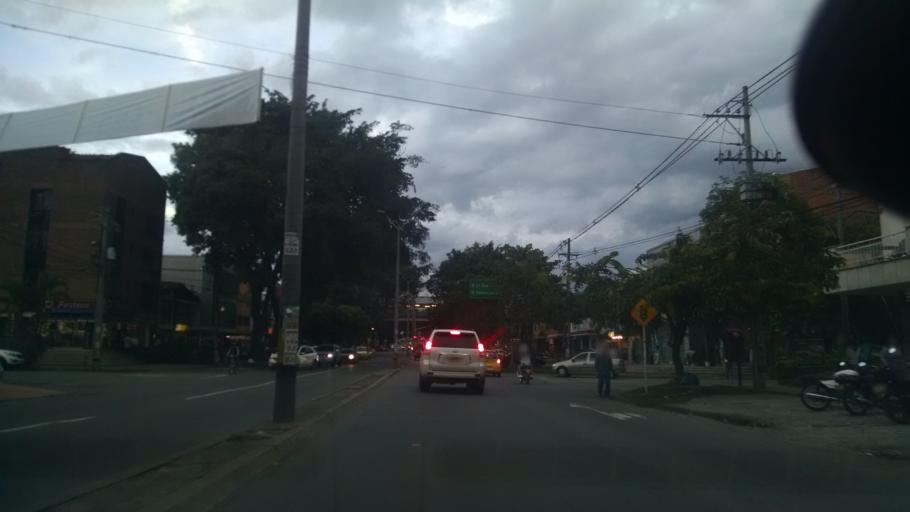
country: CO
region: Antioquia
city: Medellin
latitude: 6.2604
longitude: -75.5974
